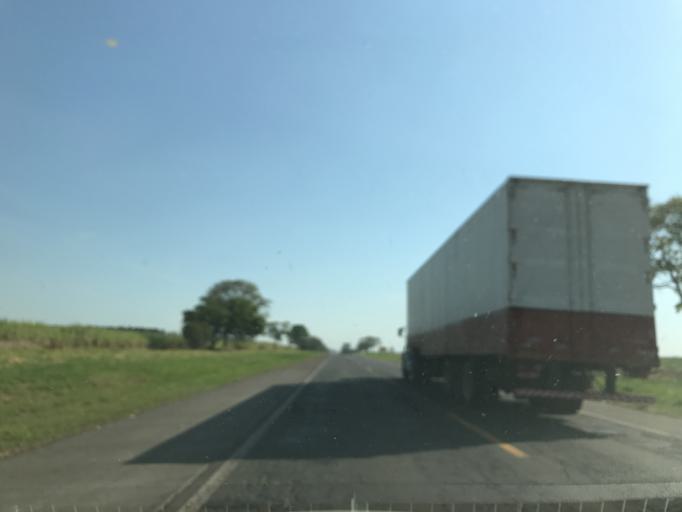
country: BR
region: Sao Paulo
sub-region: Penapolis
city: Penapolis
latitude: -21.4718
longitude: -50.1904
